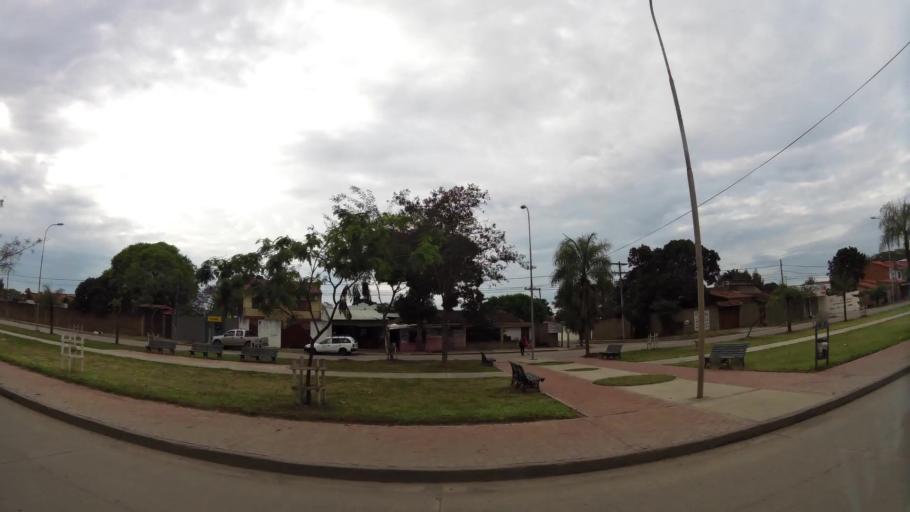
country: BO
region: Santa Cruz
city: Santa Cruz de la Sierra
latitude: -17.7408
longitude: -63.1579
